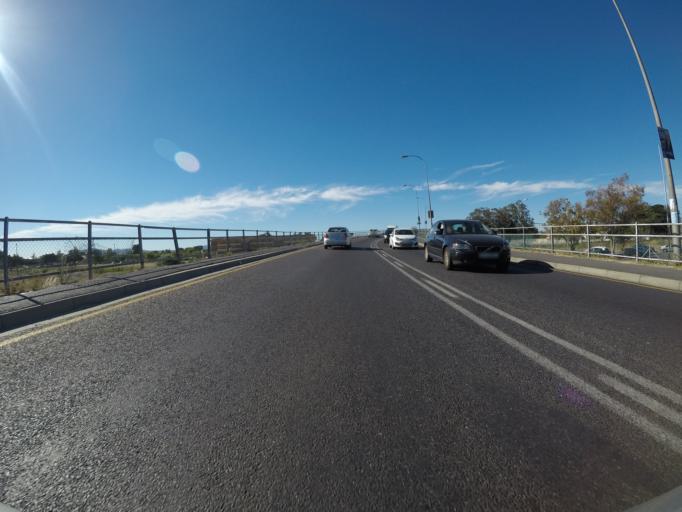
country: ZA
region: Western Cape
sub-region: City of Cape Town
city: Kraaifontein
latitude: -33.9332
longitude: 18.6758
